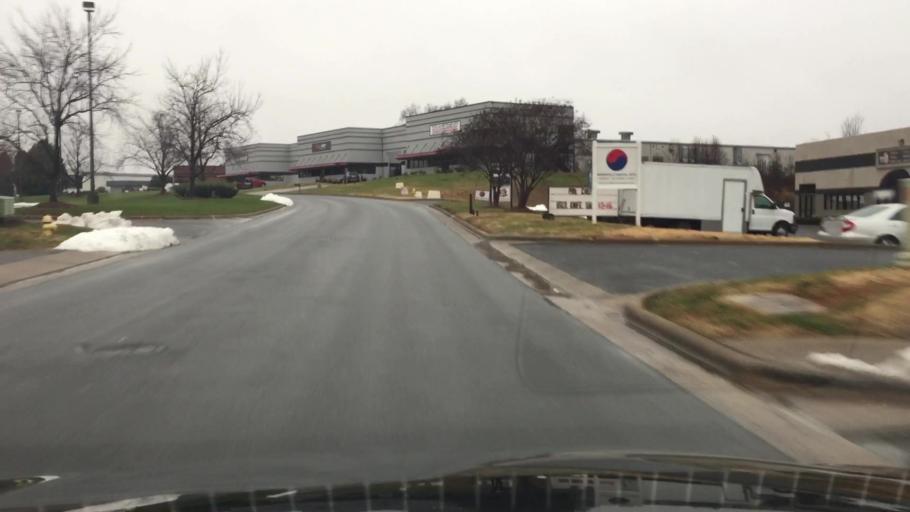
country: US
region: North Carolina
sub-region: Iredell County
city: Mooresville
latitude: 35.5869
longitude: -80.8613
